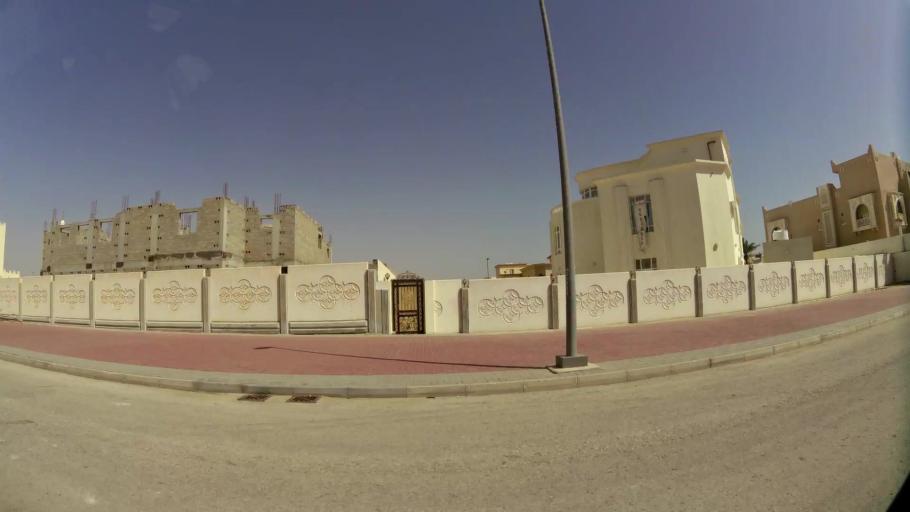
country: QA
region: Baladiyat ad Dawhah
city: Doha
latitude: 25.3601
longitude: 51.4972
